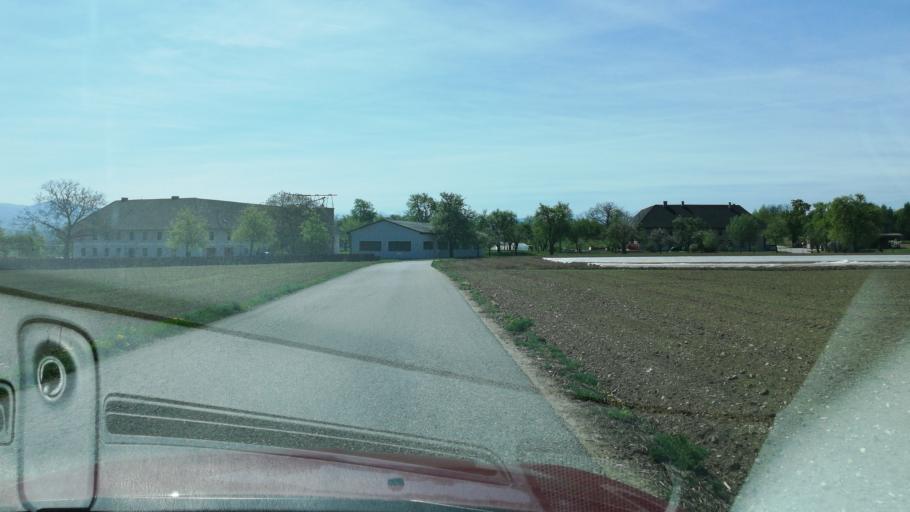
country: AT
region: Upper Austria
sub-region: Politischer Bezirk Steyr-Land
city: Pfarrkirchen bei Bad Hall
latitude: 48.0377
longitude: 14.1858
